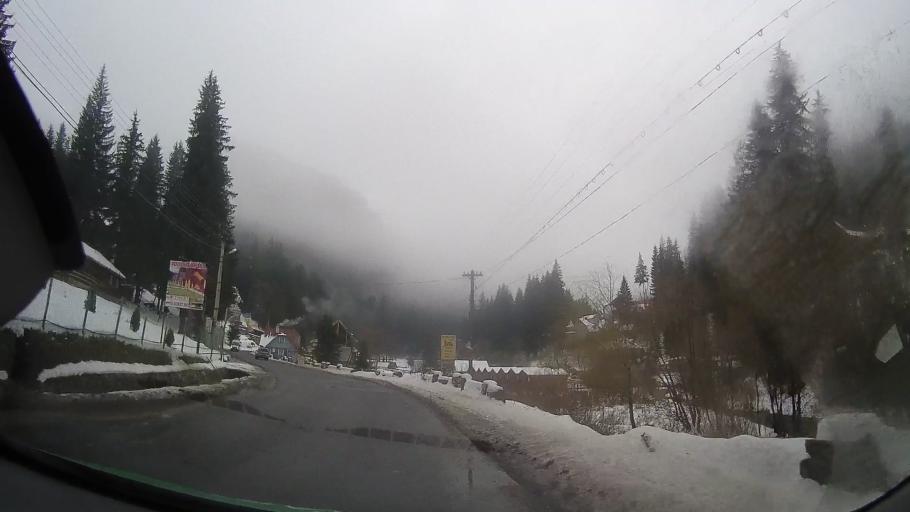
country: RO
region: Neamt
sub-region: Comuna Bicaz Chei
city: Bicaz Chei
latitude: 46.7965
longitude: 25.8016
